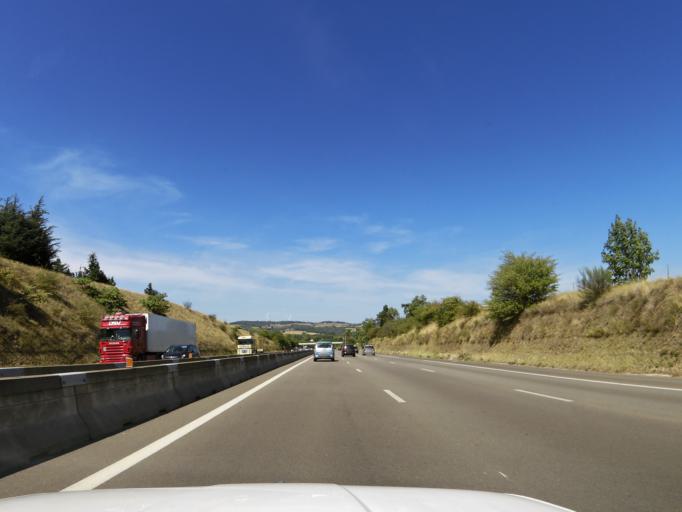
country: FR
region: Rhone-Alpes
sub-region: Departement de la Drome
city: Saint-Barthelemy-de-Vals
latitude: 45.1643
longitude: 4.8889
